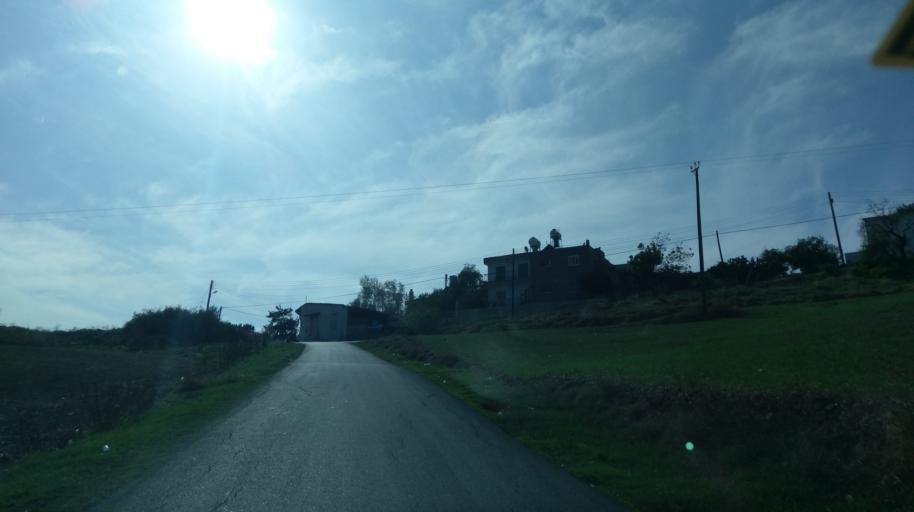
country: CY
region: Keryneia
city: Lapithos
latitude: 35.2867
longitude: 33.2393
